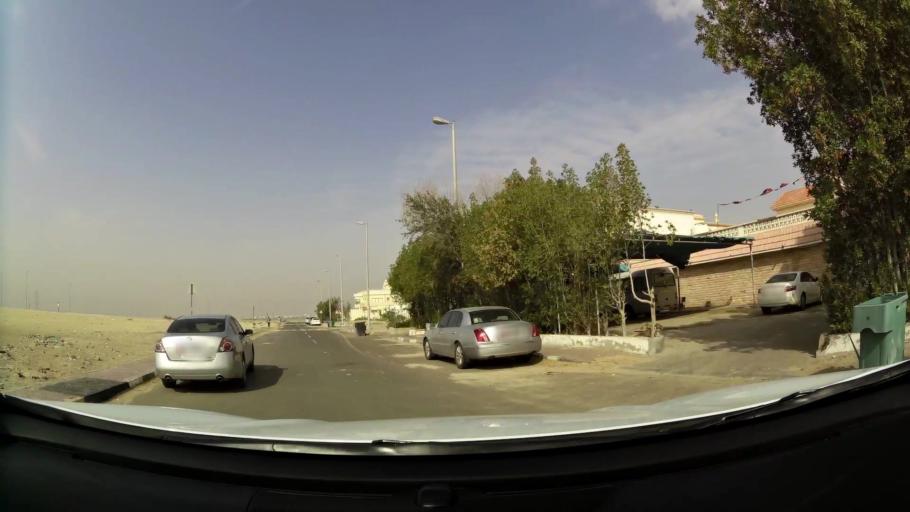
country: AE
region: Abu Dhabi
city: Abu Dhabi
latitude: 24.2618
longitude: 54.6986
